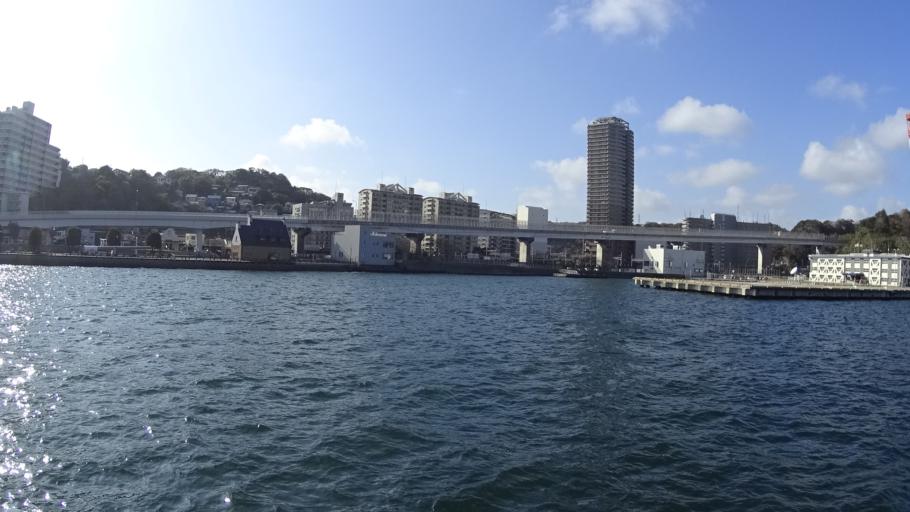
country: JP
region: Kanagawa
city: Yokosuka
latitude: 35.2860
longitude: 139.6567
